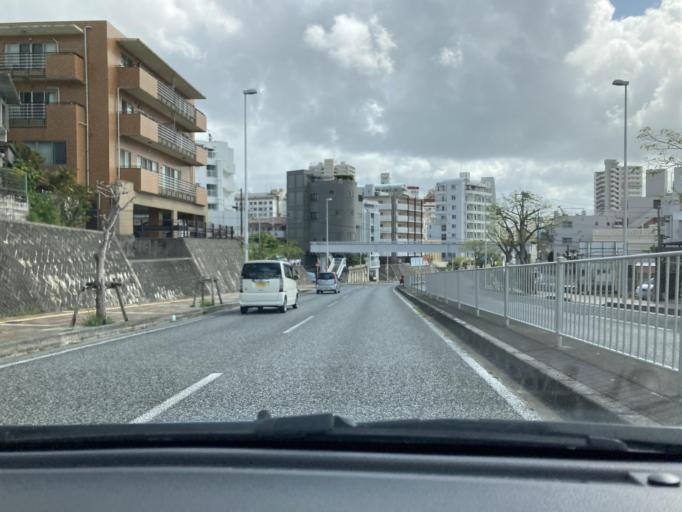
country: JP
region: Okinawa
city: Naha-shi
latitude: 26.2218
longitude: 127.6926
